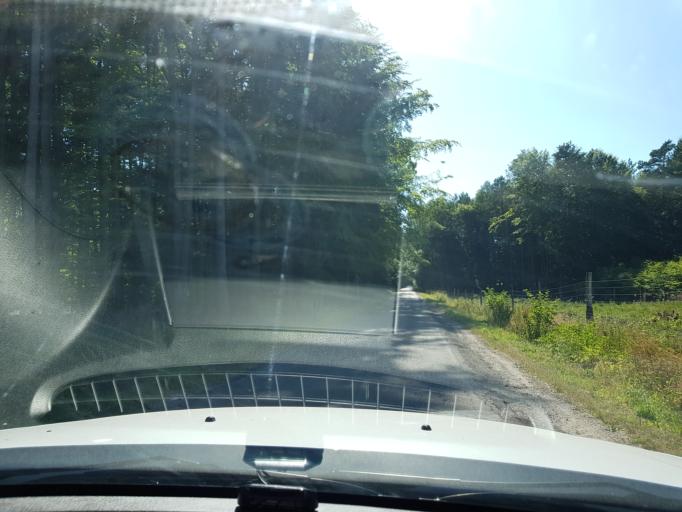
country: PL
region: West Pomeranian Voivodeship
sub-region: Powiat swidwinski
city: Slawoborze
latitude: 53.8364
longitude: 15.7075
